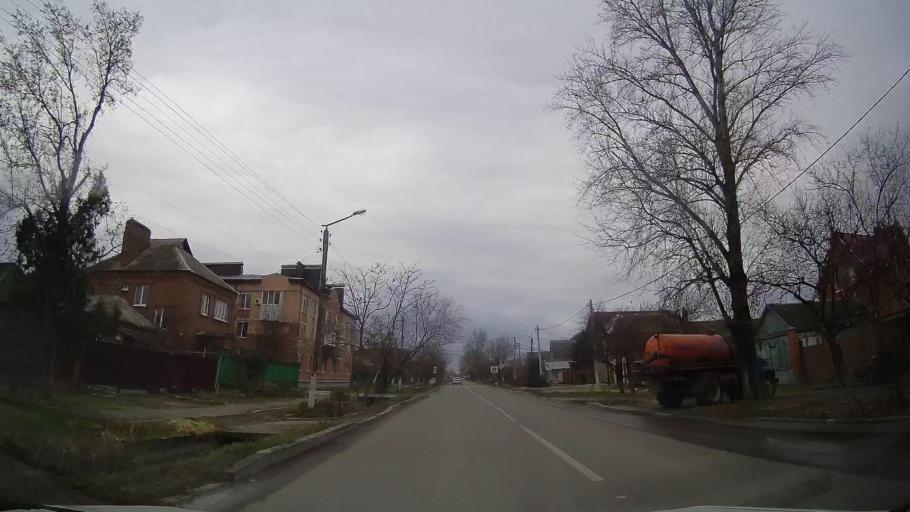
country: RU
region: Rostov
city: Bataysk
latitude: 47.1258
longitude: 39.7435
